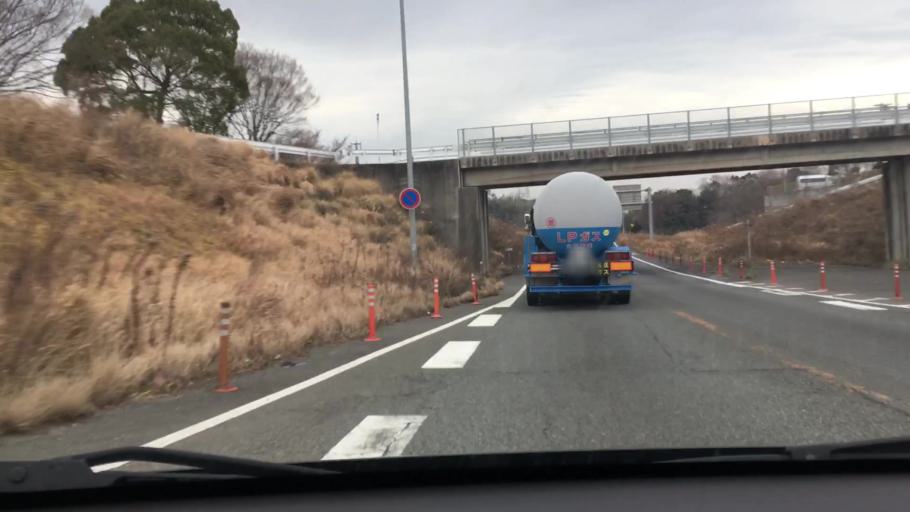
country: JP
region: Mie
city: Kameyama
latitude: 34.8633
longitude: 136.4746
